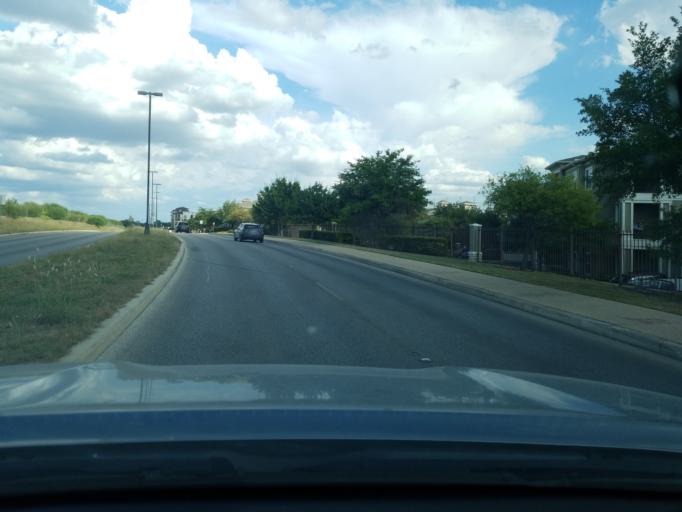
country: US
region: Texas
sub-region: Bexar County
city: Shavano Park
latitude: 29.5993
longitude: -98.5961
